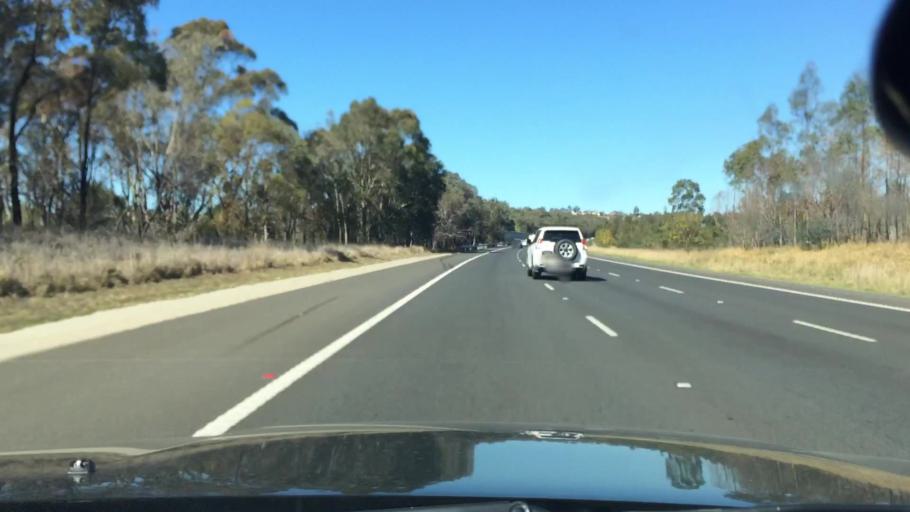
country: AU
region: New South Wales
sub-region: Campbelltown Municipality
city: Leumeah
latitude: -34.0371
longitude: 150.8238
